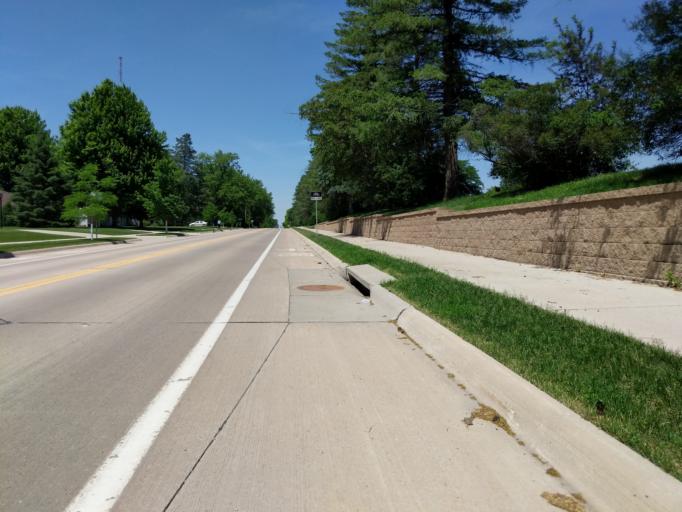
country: US
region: Iowa
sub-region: Linn County
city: Cedar Rapids
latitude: 42.0222
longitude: -91.6385
